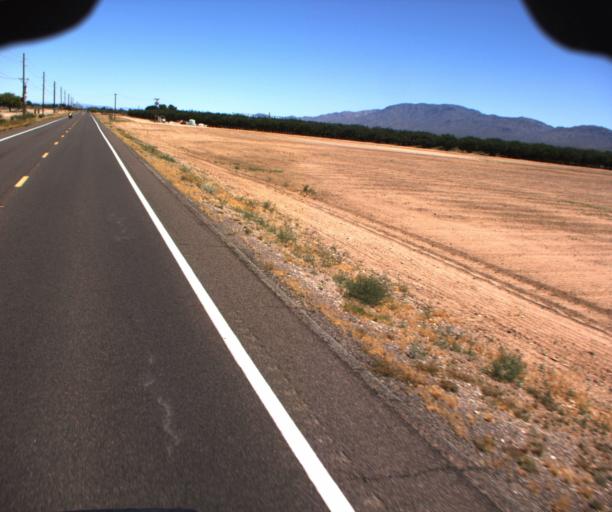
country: US
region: Arizona
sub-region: La Paz County
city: Salome
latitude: 33.8094
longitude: -113.5647
